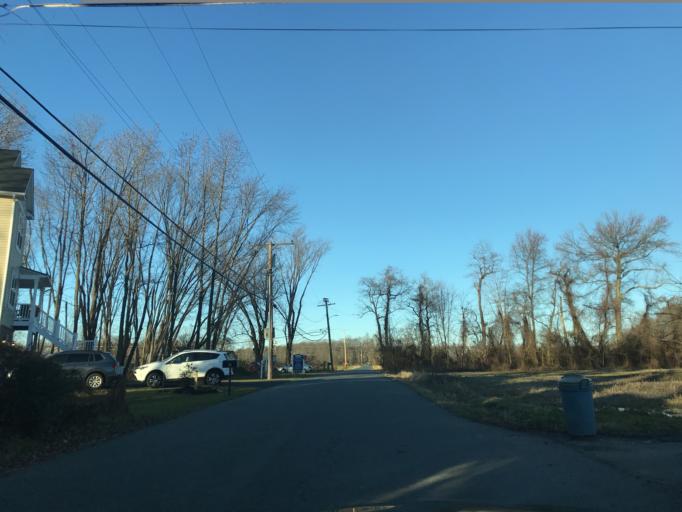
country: US
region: Maryland
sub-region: Baltimore County
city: Bowleys Quarters
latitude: 39.3252
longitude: -76.3788
